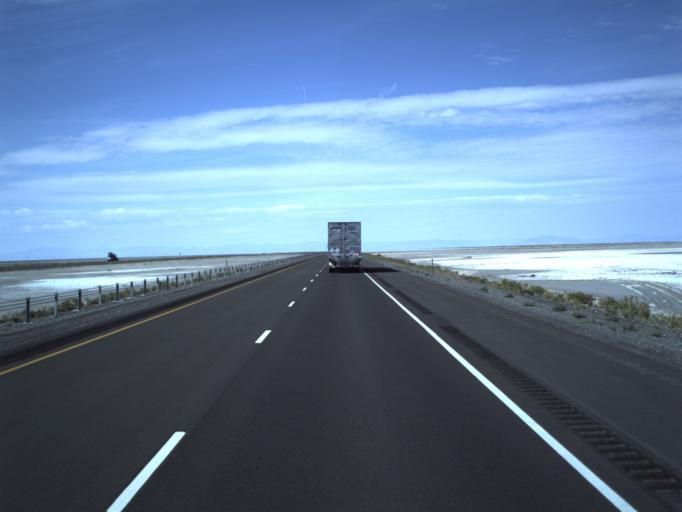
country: US
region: Utah
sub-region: Tooele County
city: Wendover
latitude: 40.7286
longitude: -113.3428
